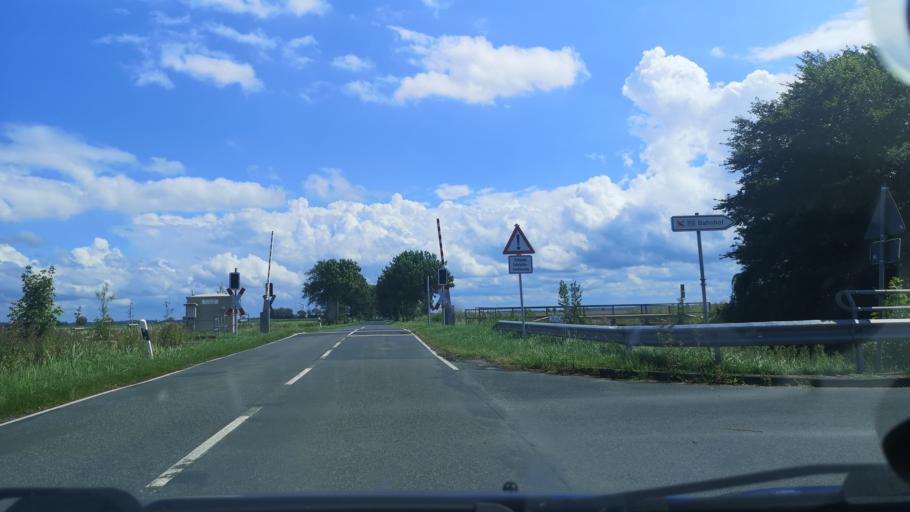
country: DE
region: Lower Saxony
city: Wremen
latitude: 53.6486
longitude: 8.5212
